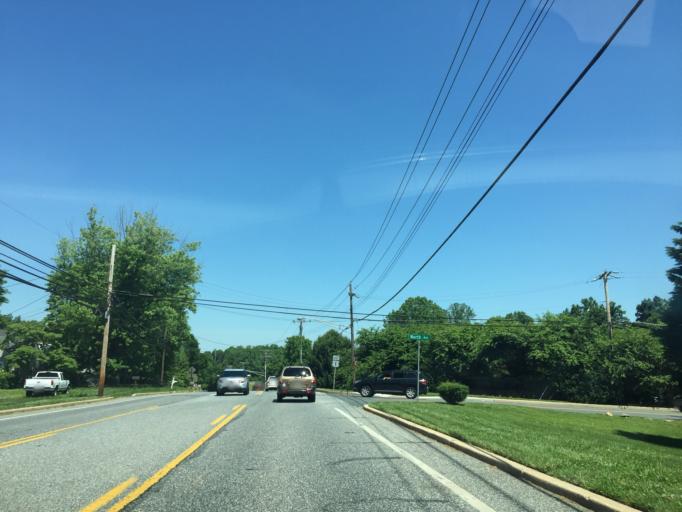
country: US
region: Maryland
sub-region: Harford County
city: Bel Air North
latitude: 39.5509
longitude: -76.3636
